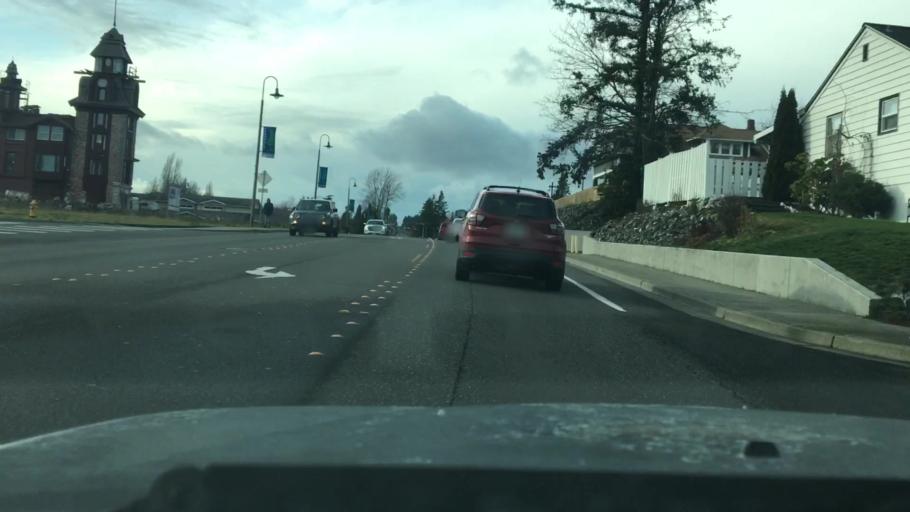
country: US
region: Washington
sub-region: Whatcom County
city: Ferndale
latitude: 48.8484
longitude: -122.5972
